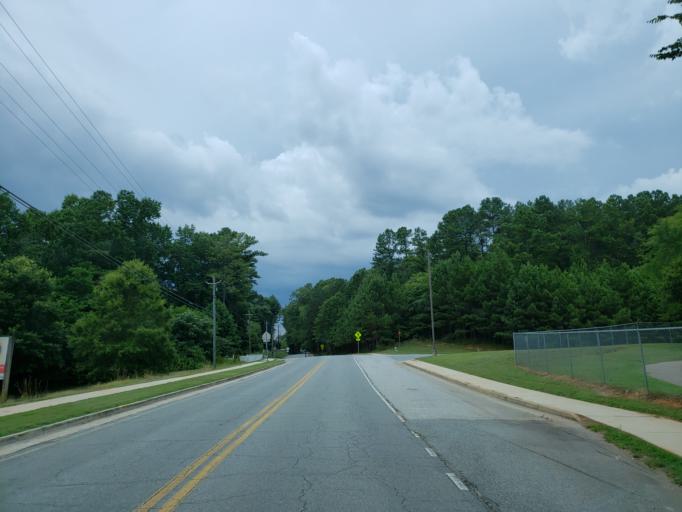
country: US
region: Georgia
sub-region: Cherokee County
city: Woodstock
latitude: 34.1087
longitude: -84.5229
